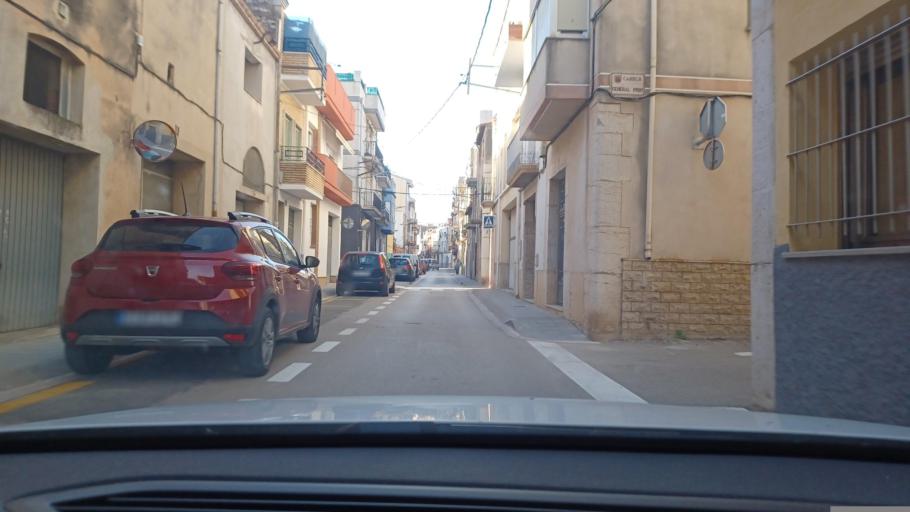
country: ES
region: Catalonia
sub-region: Provincia de Tarragona
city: Ulldecona
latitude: 40.5989
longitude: 0.4472
